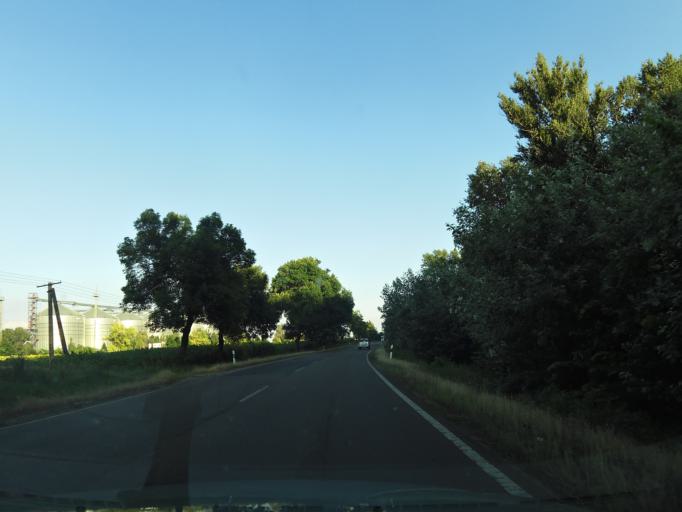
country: HU
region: Jasz-Nagykun-Szolnok
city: Rakocziujfalu
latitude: 47.0381
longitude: 20.2886
